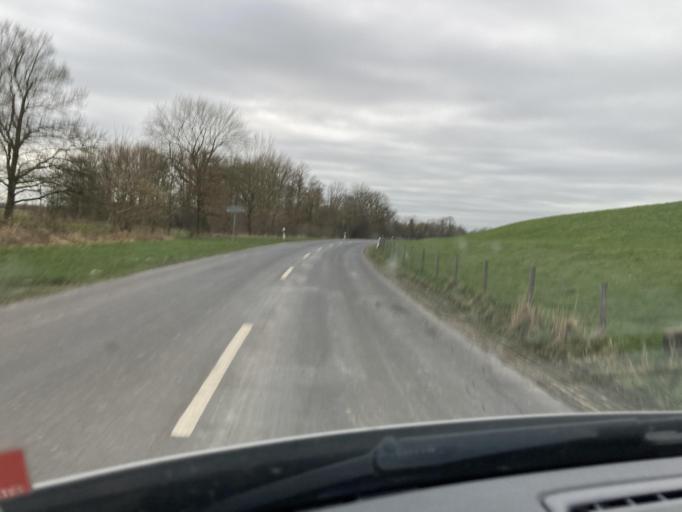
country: DE
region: Lower Saxony
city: Leer
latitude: 53.2078
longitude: 7.4306
